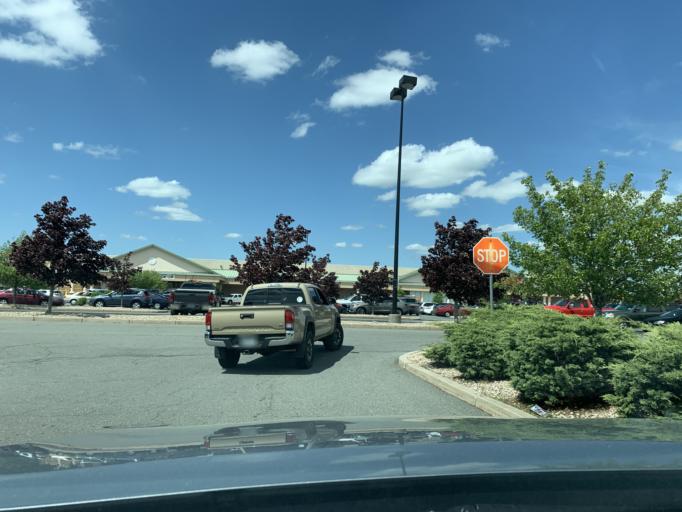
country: US
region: Rhode Island
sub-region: Kent County
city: West Warwick
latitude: 41.6620
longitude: -71.5522
